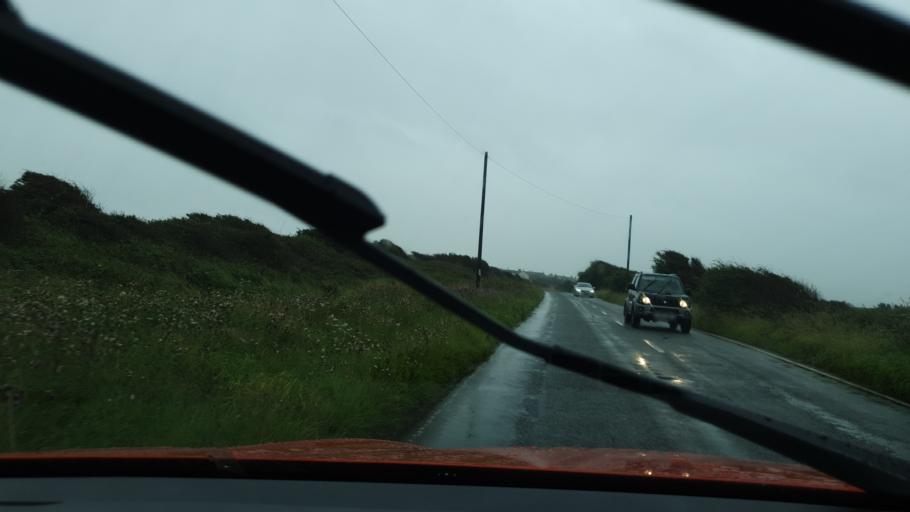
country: GB
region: England
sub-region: Cumbria
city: Barrow in Furness
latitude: 54.0885
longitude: -3.2429
